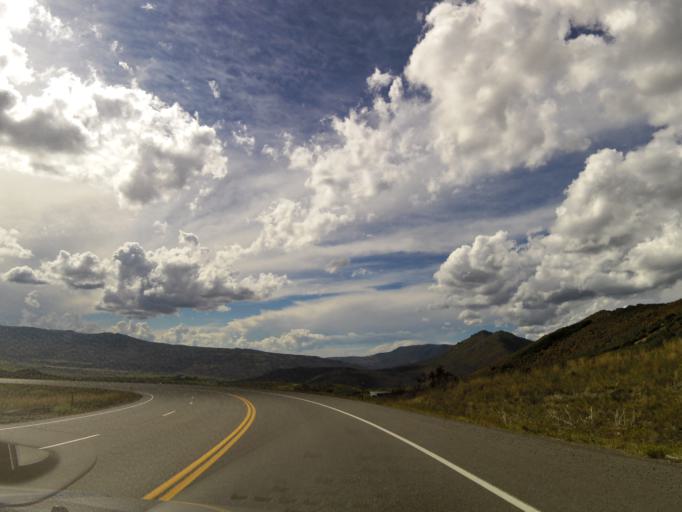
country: US
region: Colorado
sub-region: Hinsdale County
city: Lake City
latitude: 38.3968
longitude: -107.4518
